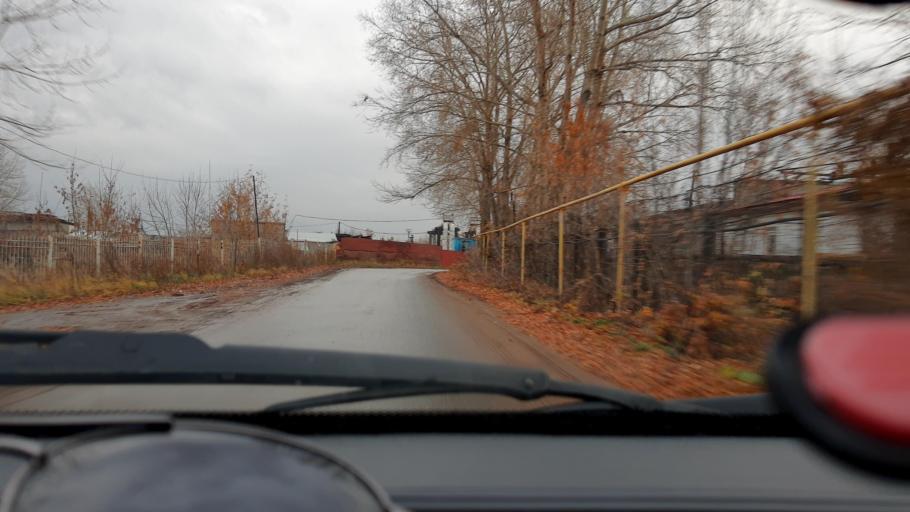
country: RU
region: Bashkortostan
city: Ufa
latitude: 54.8356
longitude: 56.1167
